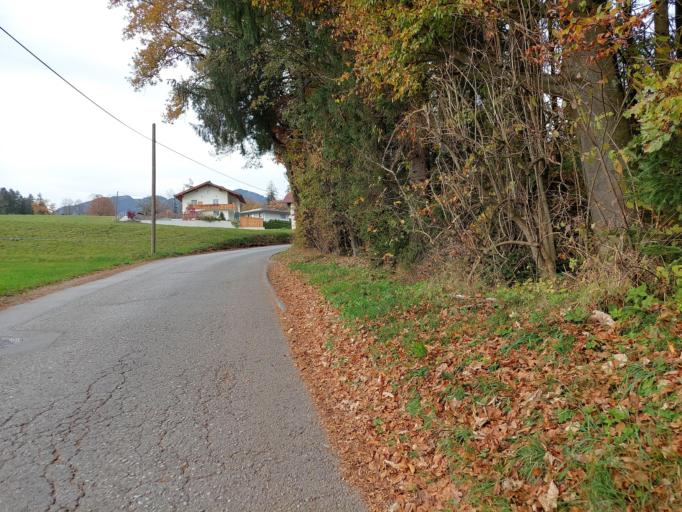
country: AT
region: Tyrol
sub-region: Politischer Bezirk Kufstein
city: Angath
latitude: 47.4988
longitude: 12.0487
